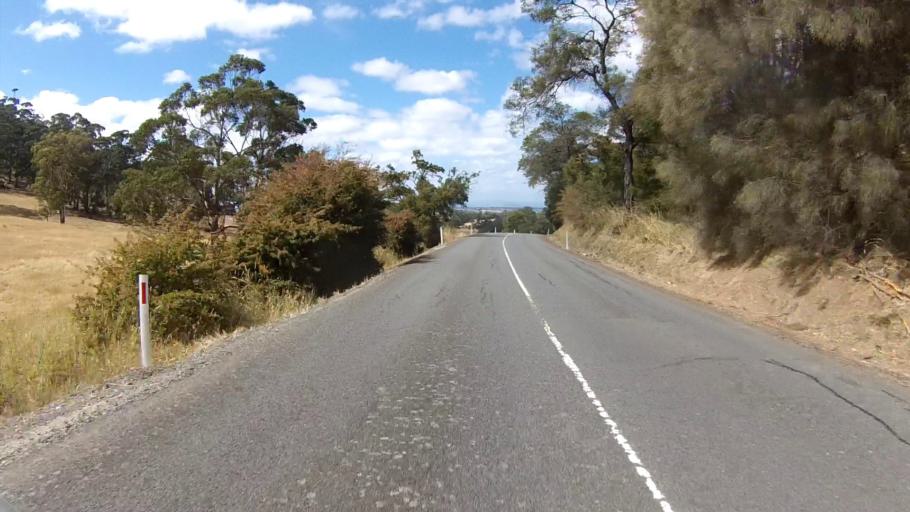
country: AU
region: Tasmania
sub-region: Sorell
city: Sorell
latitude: -42.7376
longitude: 147.4821
